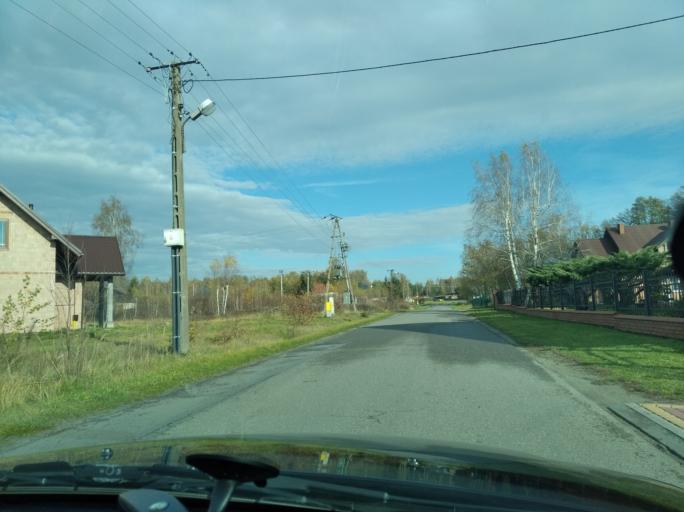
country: PL
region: Subcarpathian Voivodeship
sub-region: Powiat ropczycko-sedziszowski
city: Sedziszow Malopolski
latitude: 50.0992
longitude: 21.6597
